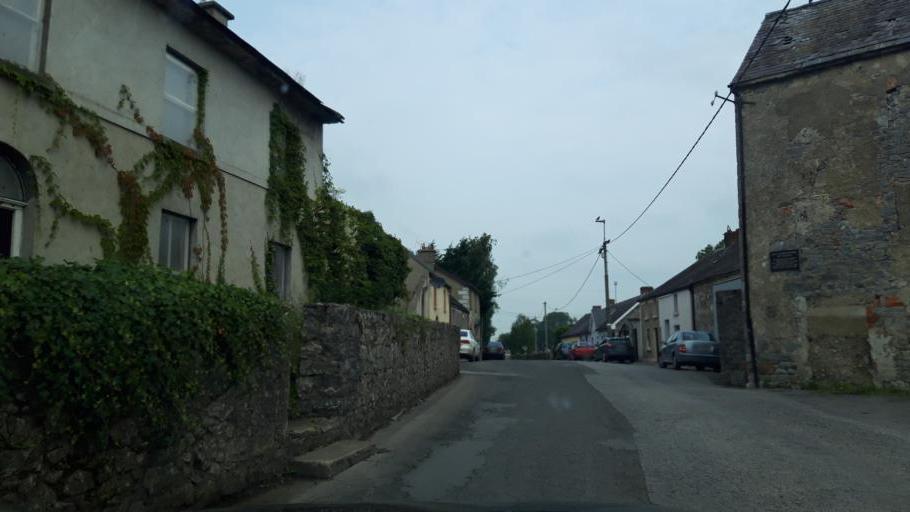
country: IE
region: Leinster
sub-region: Kilkenny
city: Callan
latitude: 52.5126
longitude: -7.5062
